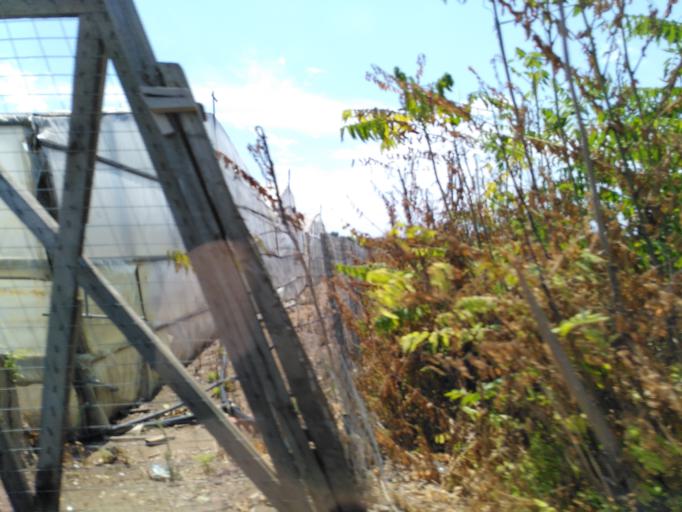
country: GR
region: Central Macedonia
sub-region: Nomos Thessalonikis
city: Agia Triada
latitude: 40.4925
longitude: 22.8600
